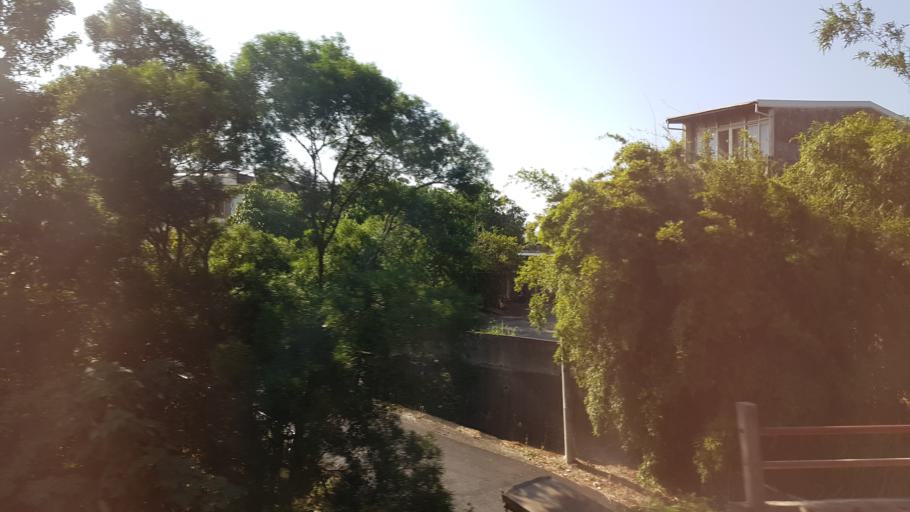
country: TW
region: Taiwan
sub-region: Miaoli
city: Miaoli
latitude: 24.6542
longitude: 120.8763
